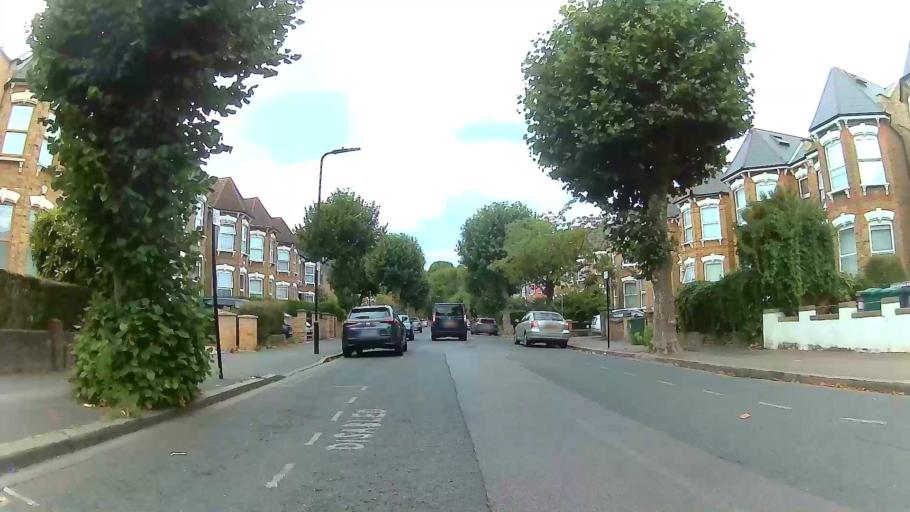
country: GB
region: England
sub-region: Greater London
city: Harringay
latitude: 51.5694
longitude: -0.0844
